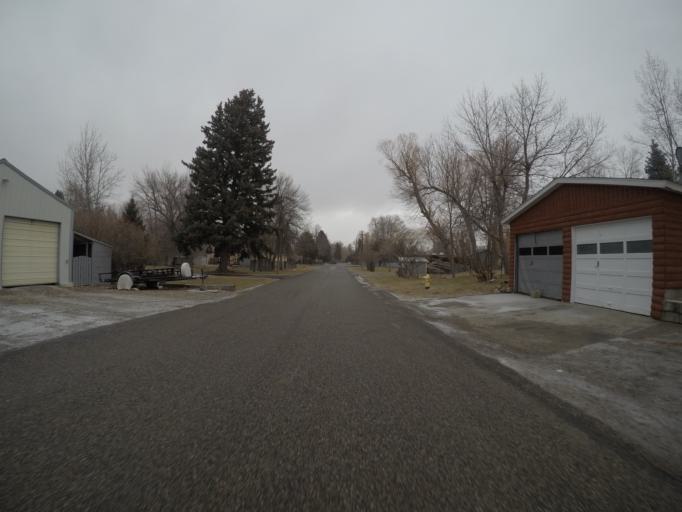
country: US
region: Montana
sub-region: Stillwater County
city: Absarokee
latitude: 45.5174
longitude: -109.4476
